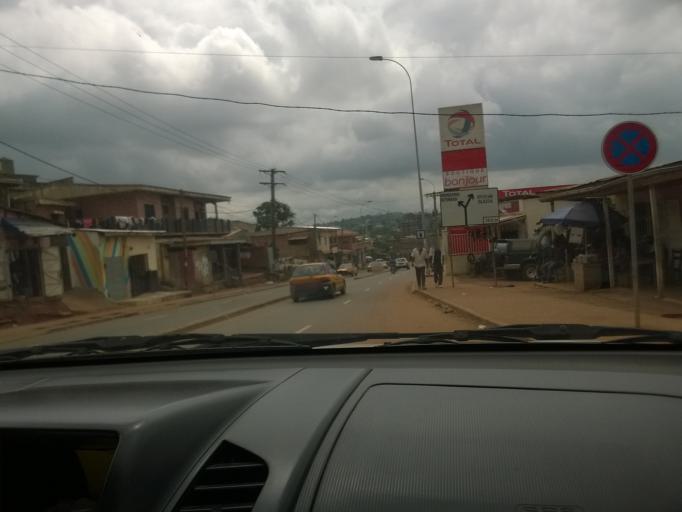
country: CM
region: Centre
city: Yaounde
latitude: 3.8342
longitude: 11.4942
